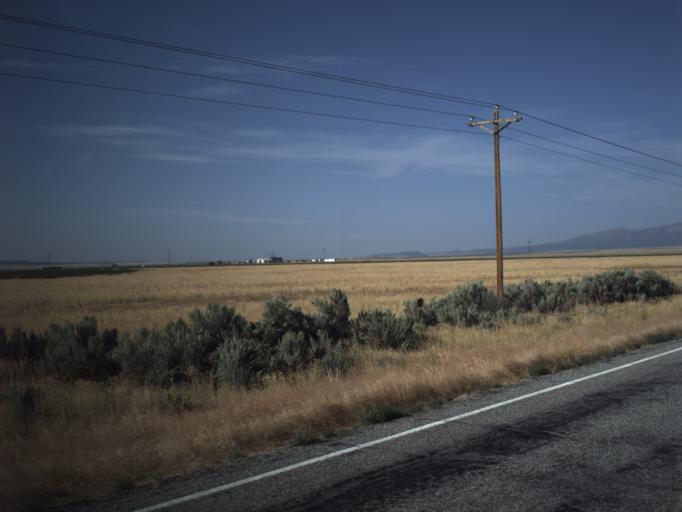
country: US
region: Idaho
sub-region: Oneida County
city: Malad City
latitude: 41.9663
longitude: -112.9368
